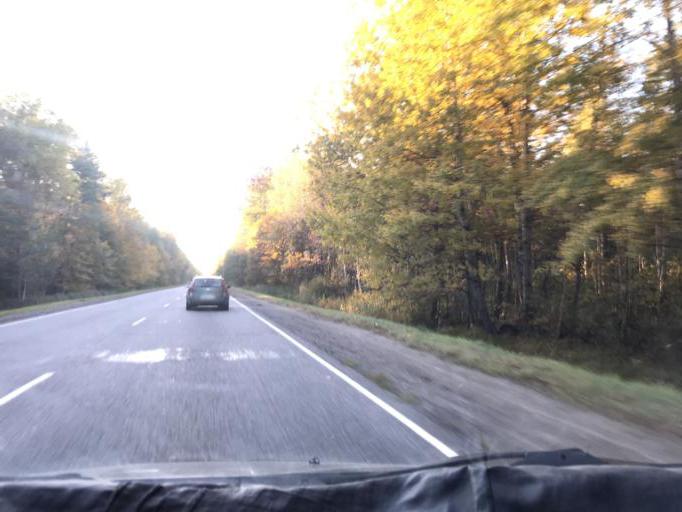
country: BY
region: Gomel
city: Zhytkavichy
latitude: 52.2733
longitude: 28.1068
